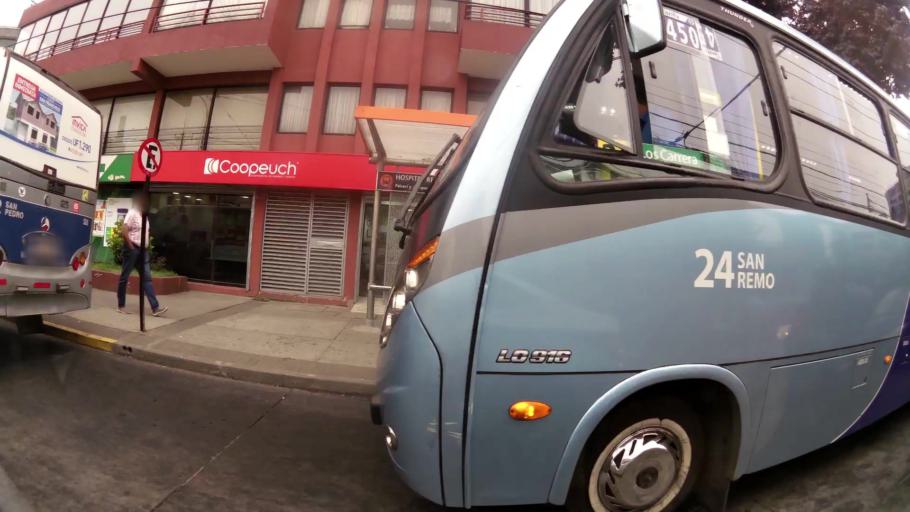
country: CL
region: Biobio
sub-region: Provincia de Concepcion
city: Concepcion
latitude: -36.8248
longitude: -73.0400
